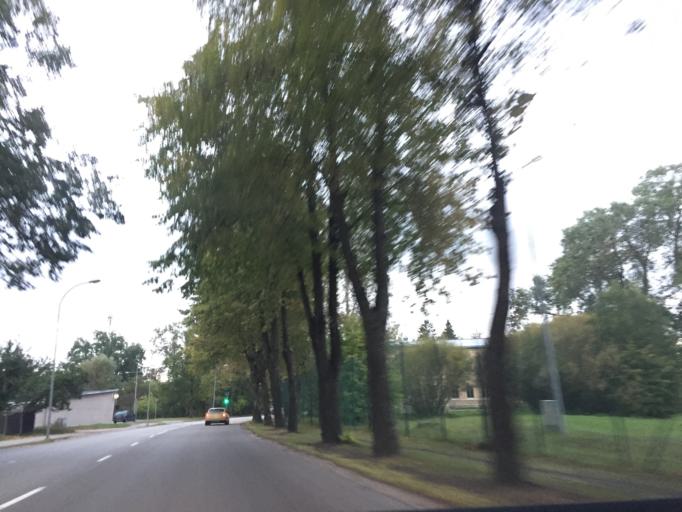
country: LV
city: Tireli
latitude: 56.9502
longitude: 23.6120
